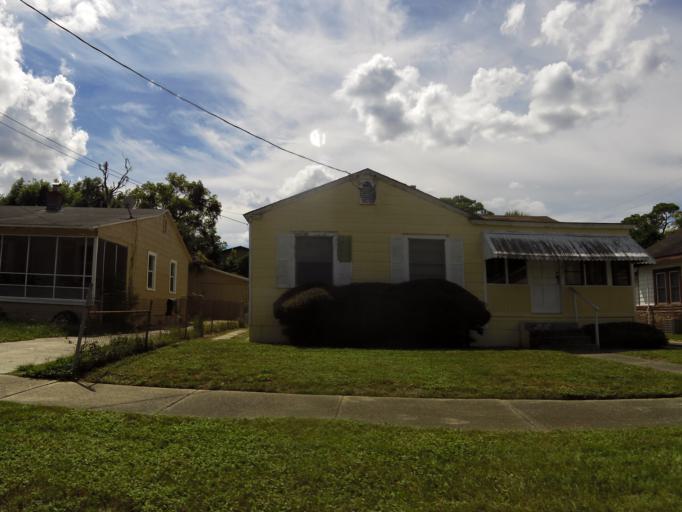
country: US
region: Florida
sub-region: Duval County
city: Jacksonville
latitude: 30.3861
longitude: -81.6454
